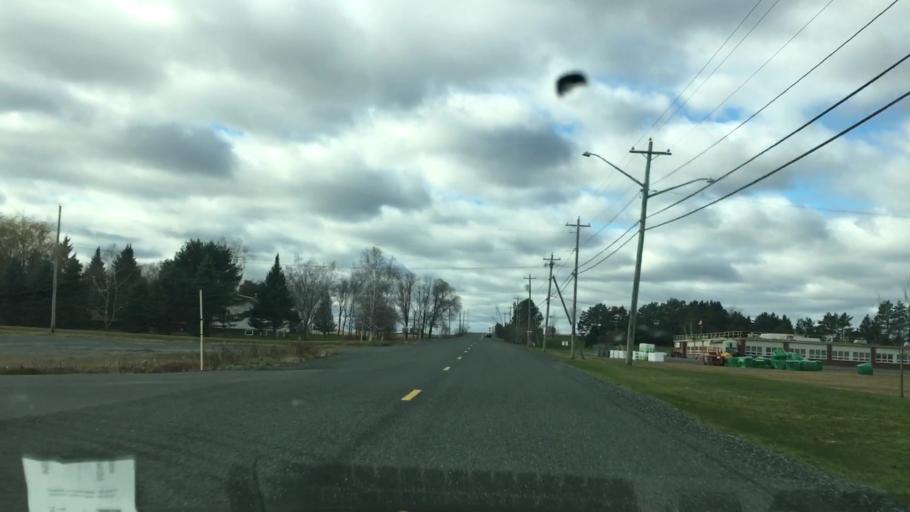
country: CA
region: New Brunswick
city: Florenceville-Bristol
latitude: 46.2883
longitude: -67.5438
